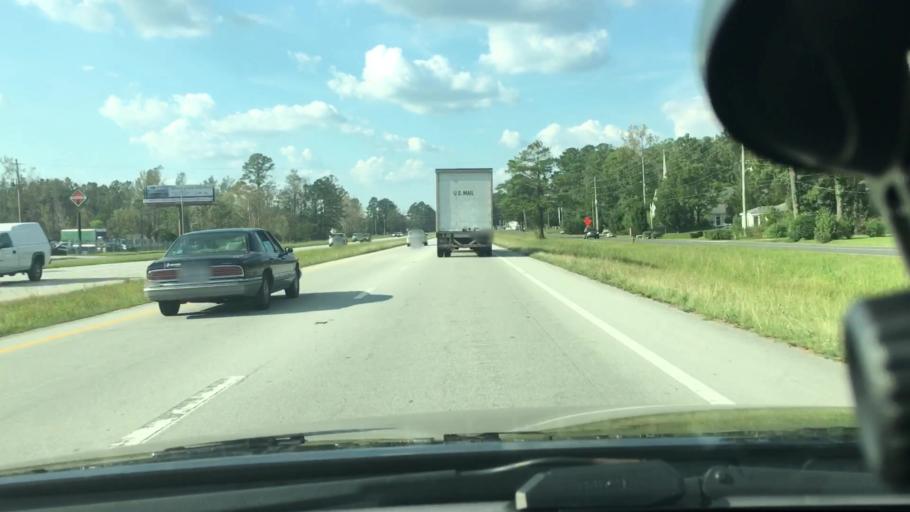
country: US
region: North Carolina
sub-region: Craven County
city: Neuse Forest
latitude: 35.0095
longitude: -76.9915
